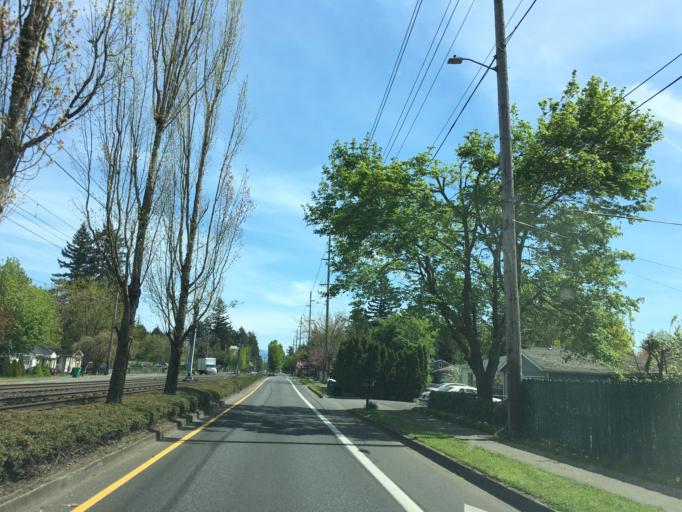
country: US
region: Oregon
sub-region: Multnomah County
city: Fairview
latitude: 45.5221
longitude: -122.4907
